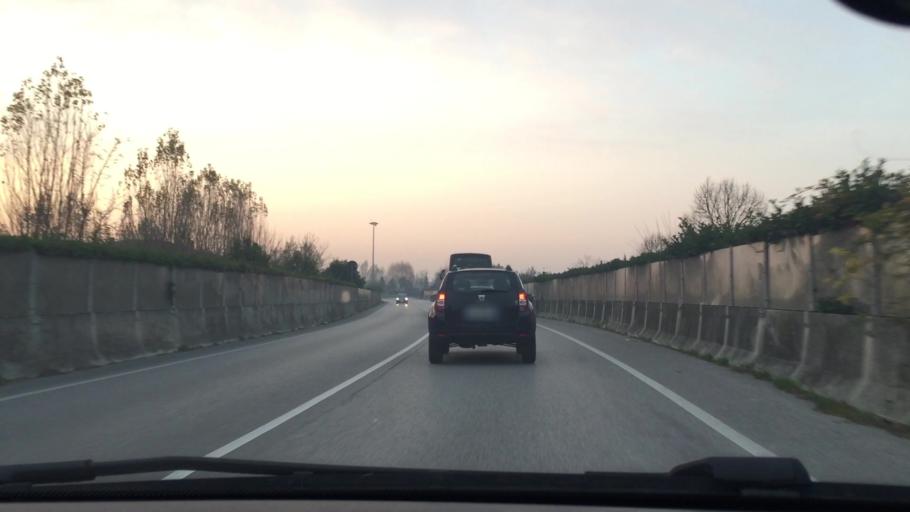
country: IT
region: Veneto
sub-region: Provincia di Venezia
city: Cavarzere
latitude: 45.1342
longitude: 12.0705
